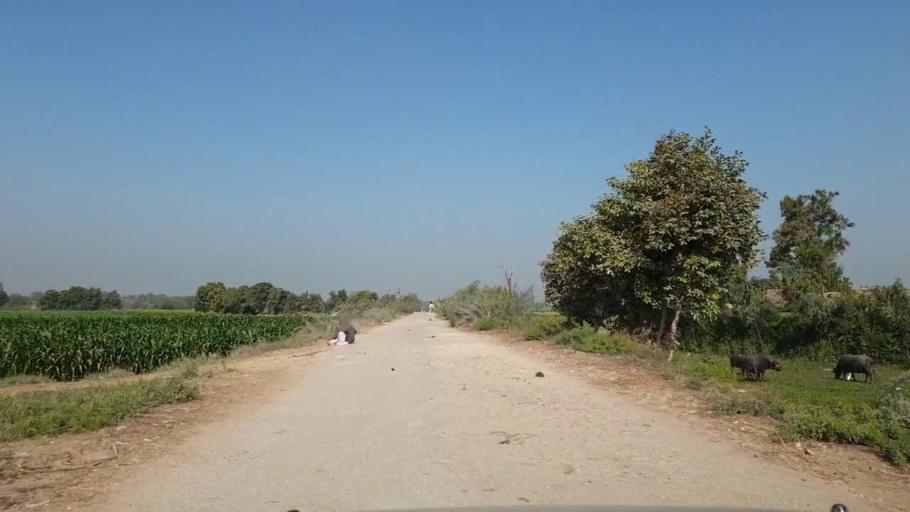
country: PK
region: Sindh
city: Matiari
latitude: 25.5790
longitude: 68.6041
